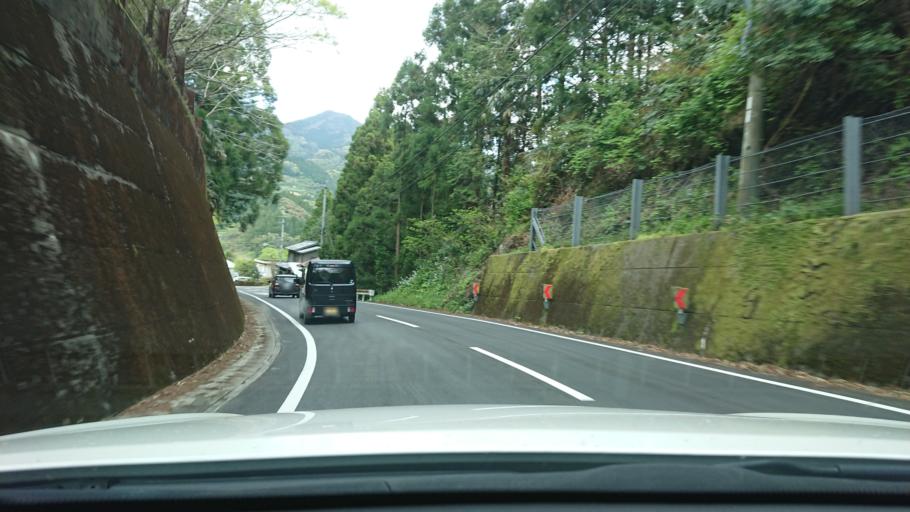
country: JP
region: Tokushima
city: Ishii
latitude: 33.9174
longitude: 134.4266
